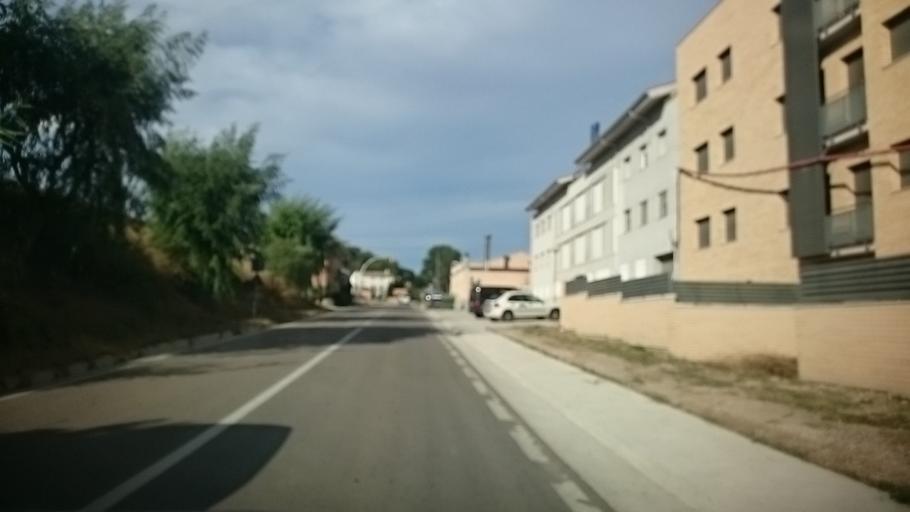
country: ES
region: Catalonia
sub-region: Provincia de Barcelona
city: Odena
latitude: 41.6091
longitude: 1.6445
